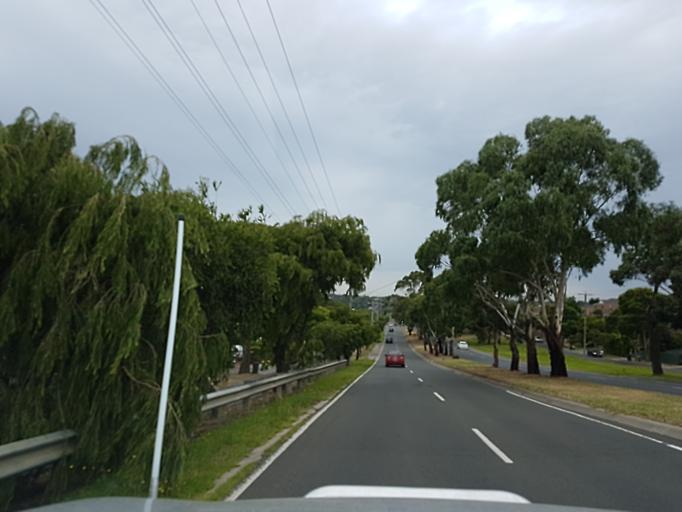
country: AU
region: Victoria
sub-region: Knox
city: Bayswater
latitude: -37.8590
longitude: 145.2623
